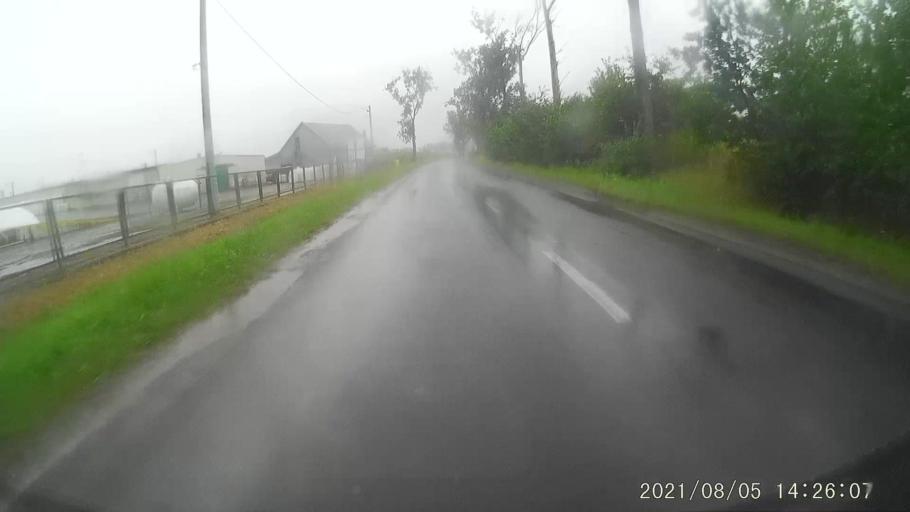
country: PL
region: Opole Voivodeship
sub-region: Powiat nyski
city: Korfantow
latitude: 50.4868
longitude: 17.6056
